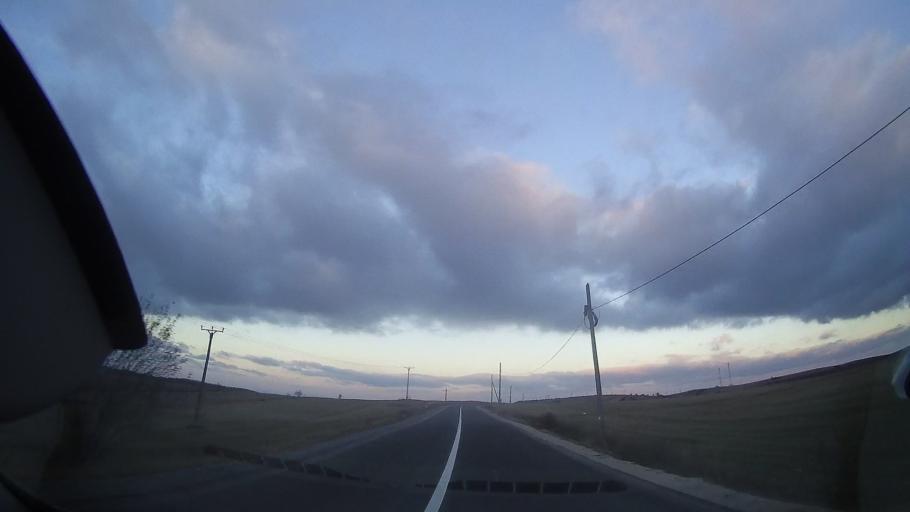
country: RO
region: Cluj
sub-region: Comuna Izvoru Crisului
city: Izvoru Crisului
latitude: 46.8150
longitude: 23.1383
